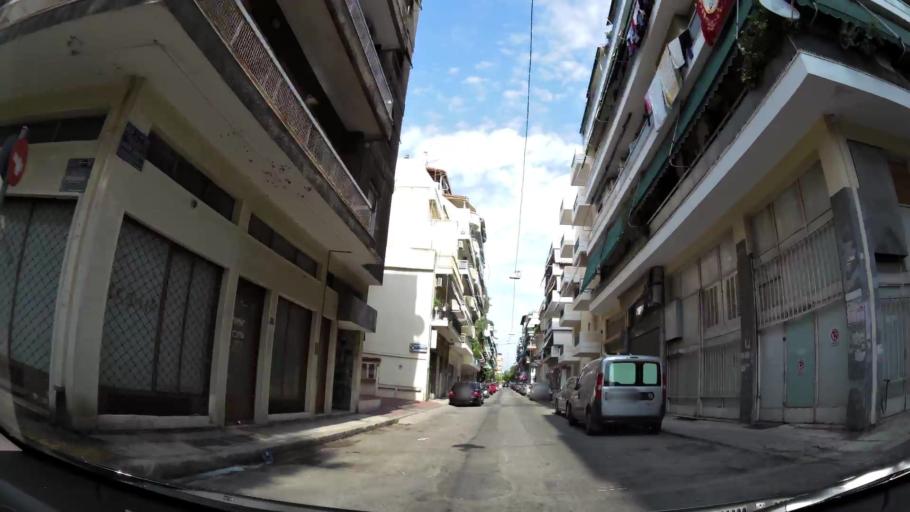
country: GR
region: Attica
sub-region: Nomarchia Athinas
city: Athens
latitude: 37.9903
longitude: 23.7180
